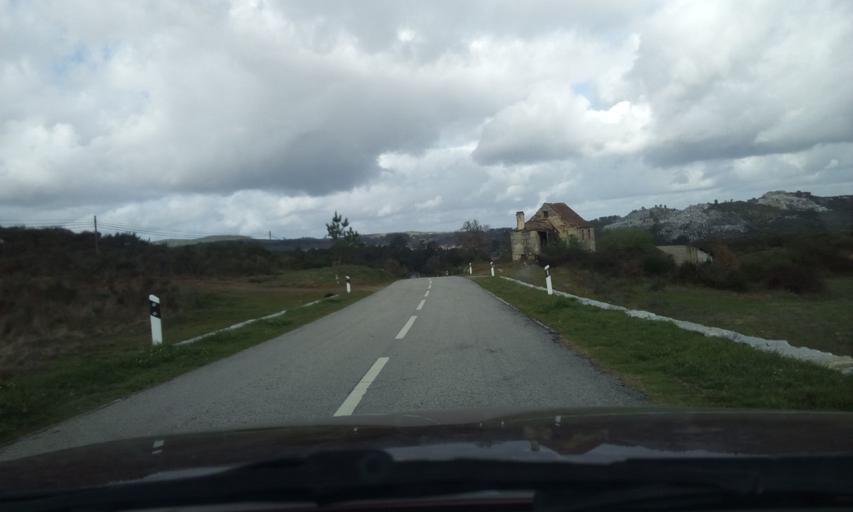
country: PT
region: Guarda
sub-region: Fornos de Algodres
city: Fornos de Algodres
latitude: 40.6542
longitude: -7.5507
